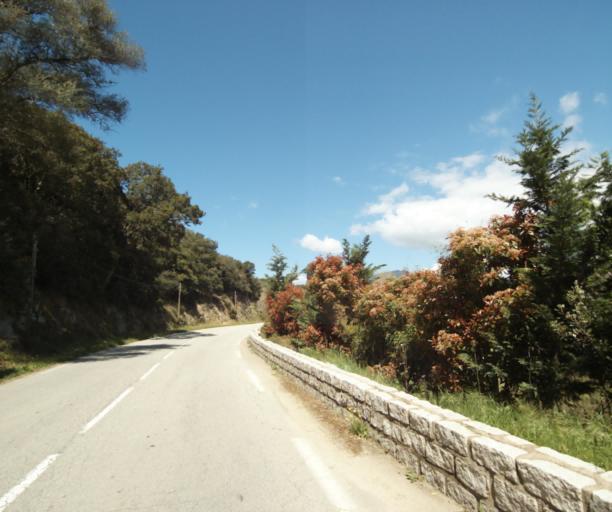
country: FR
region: Corsica
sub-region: Departement de la Corse-du-Sud
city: Propriano
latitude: 41.6572
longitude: 8.9161
